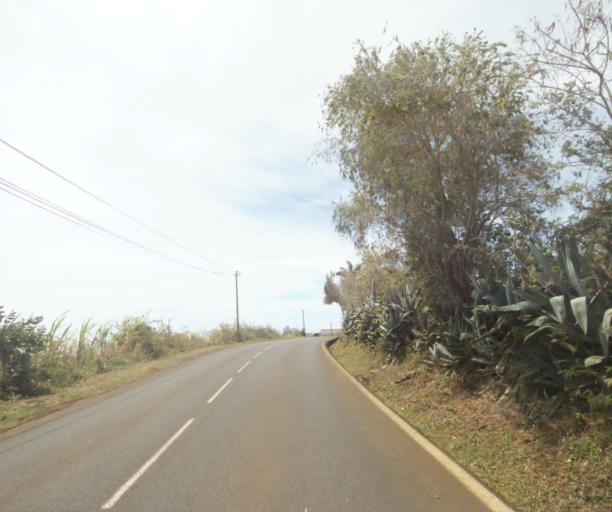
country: RE
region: Reunion
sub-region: Reunion
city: Saint-Paul
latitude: -21.0425
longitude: 55.2877
